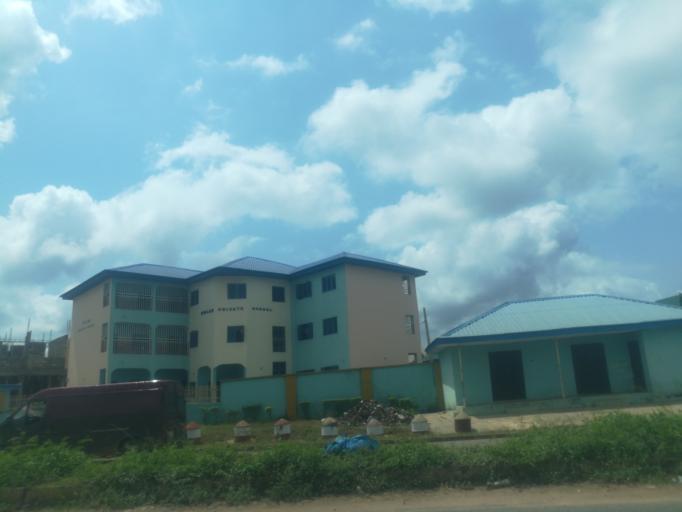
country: NG
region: Oyo
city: Ibadan
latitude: 7.3627
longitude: 3.8241
